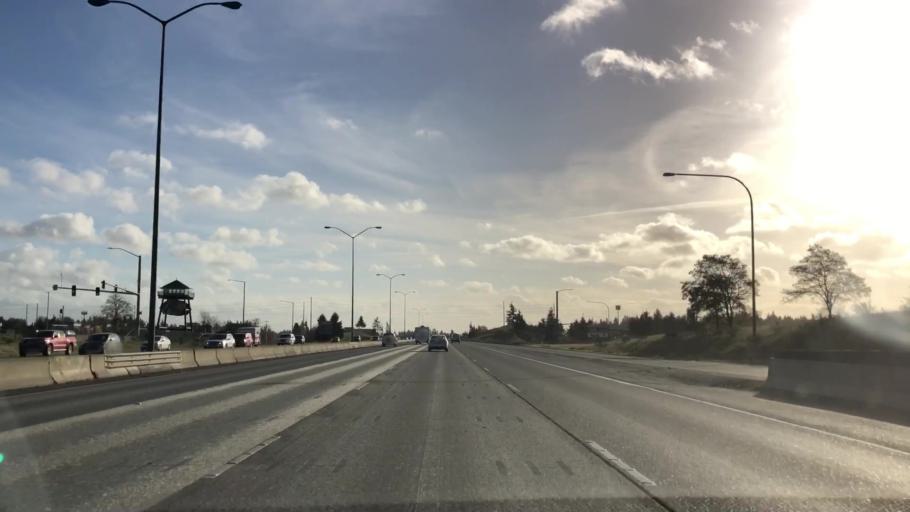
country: US
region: Washington
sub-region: Pierce County
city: Parkland
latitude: 47.1882
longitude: -122.4621
